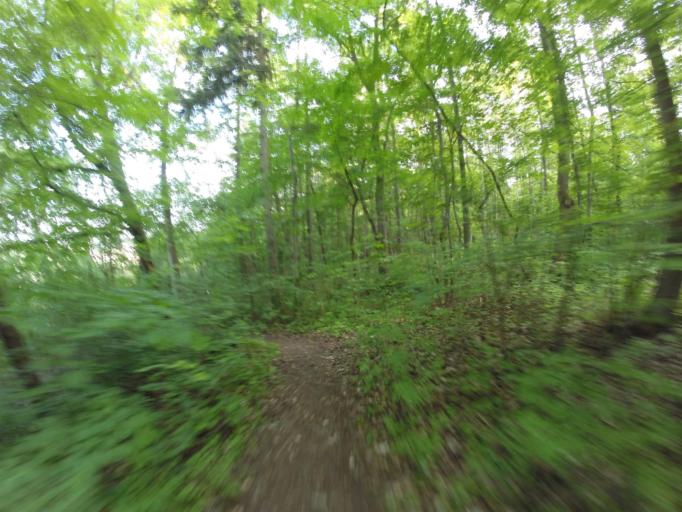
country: DE
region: Thuringia
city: Jena
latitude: 50.9413
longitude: 11.5772
